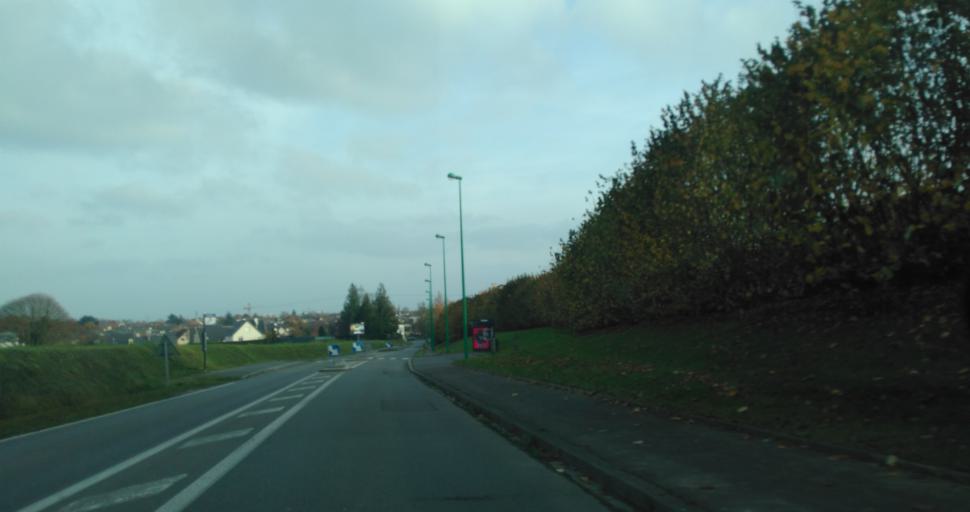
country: FR
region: Brittany
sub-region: Departement d'Ille-et-Vilaine
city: Vezin-le-Coquet
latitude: 48.1205
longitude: -1.7663
